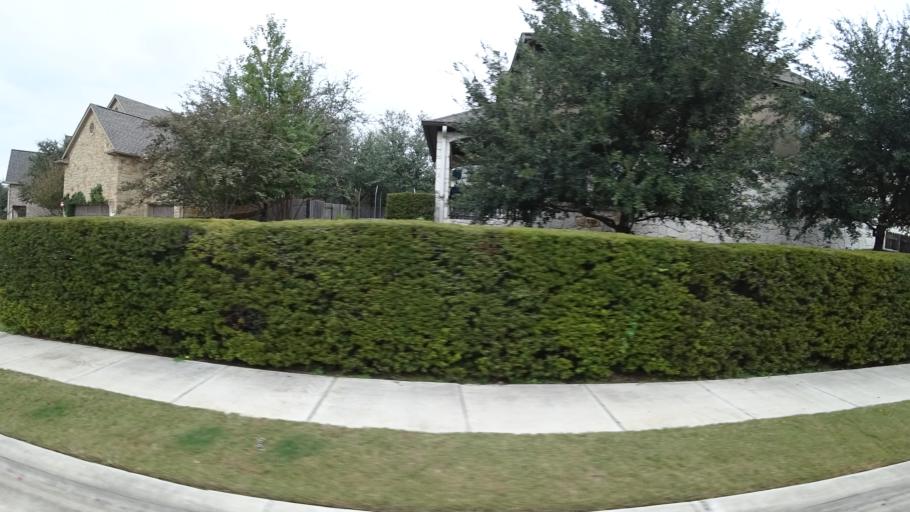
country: US
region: Texas
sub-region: Travis County
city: Bee Cave
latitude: 30.3419
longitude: -97.9086
